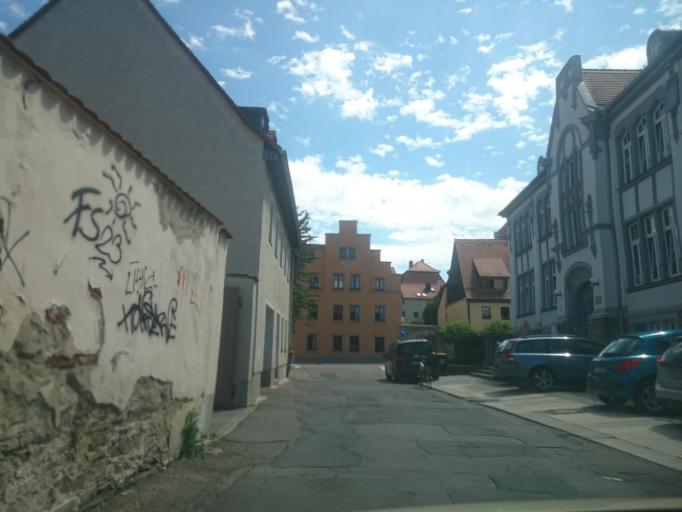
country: DE
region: Saxony
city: Freiberg
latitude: 50.9196
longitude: 13.3459
